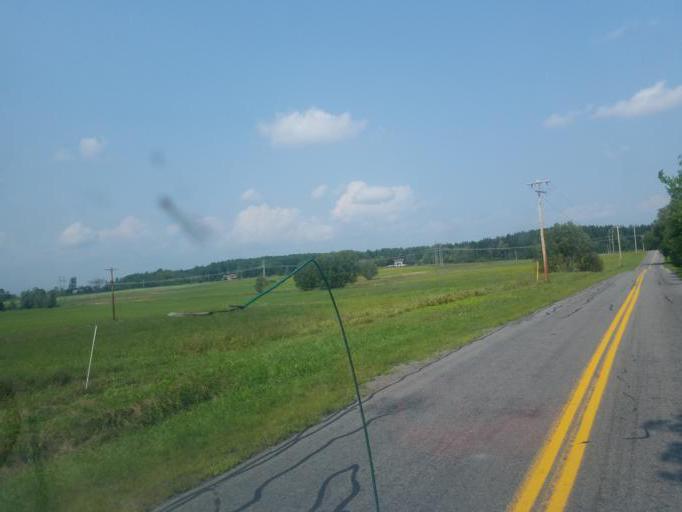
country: US
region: New York
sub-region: Montgomery County
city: Fonda
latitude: 42.8590
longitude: -74.3673
